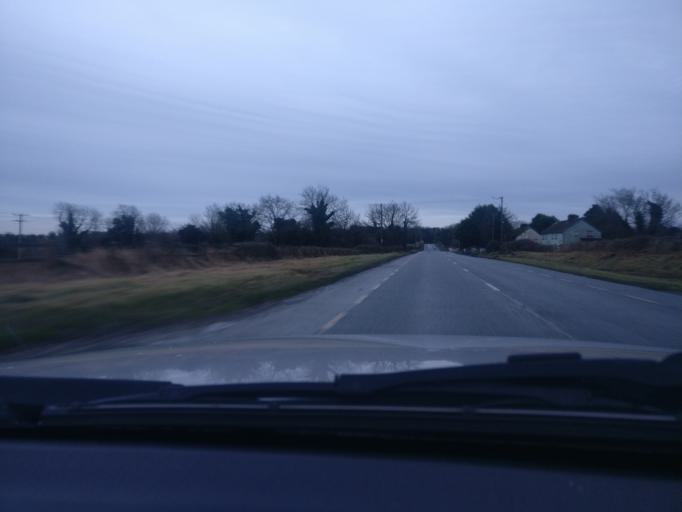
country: IE
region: Leinster
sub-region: An Mhi
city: Navan
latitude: 53.6643
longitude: -6.7264
